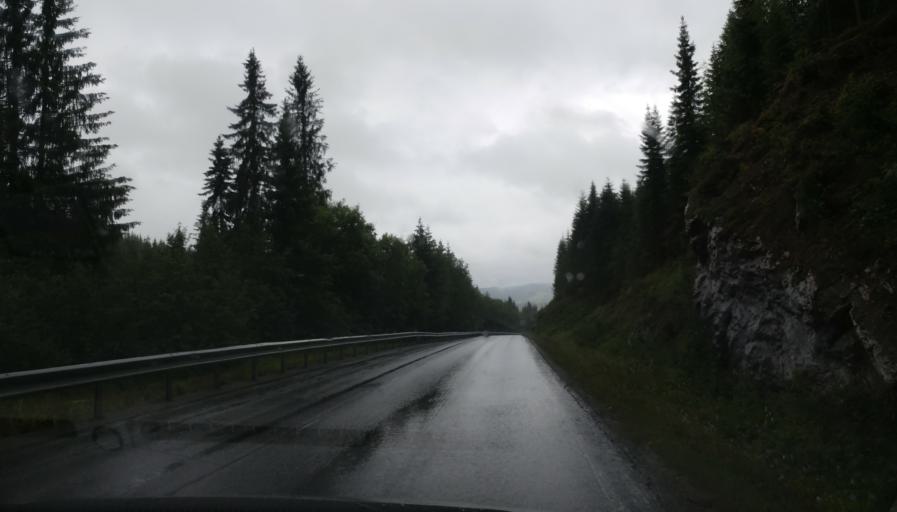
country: NO
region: Sor-Trondelag
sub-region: Selbu
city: Mebonden
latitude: 63.3041
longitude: 11.0786
